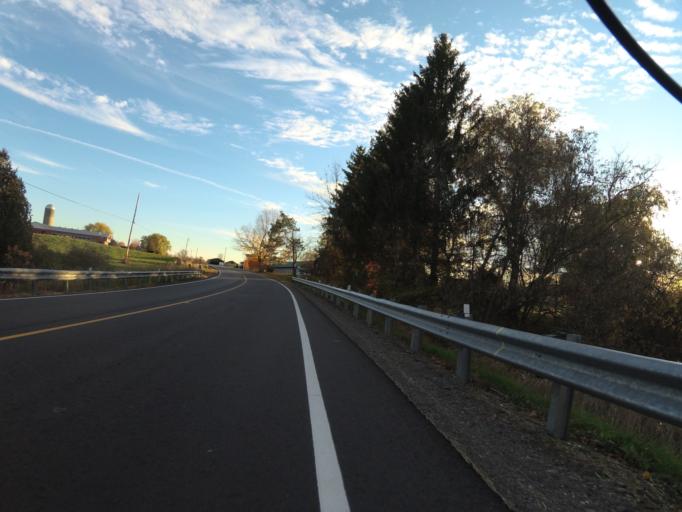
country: CA
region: Ontario
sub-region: Lanark County
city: Smiths Falls
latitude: 44.9566
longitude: -75.8130
